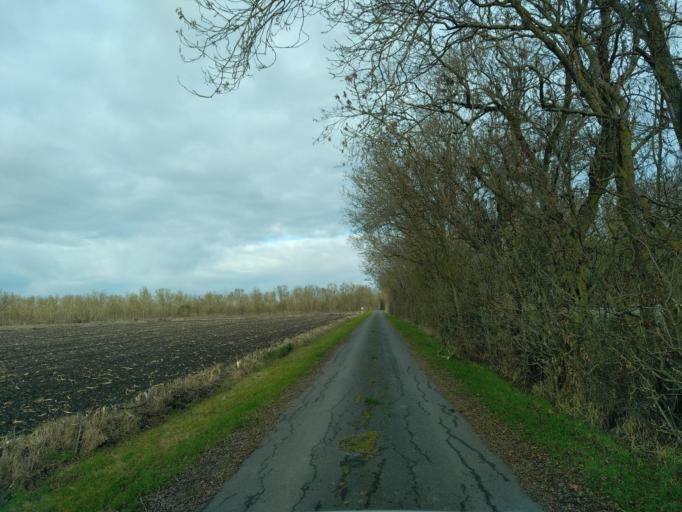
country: FR
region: Pays de la Loire
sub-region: Departement de la Vendee
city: Maillezais
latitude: 46.3258
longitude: -0.7952
